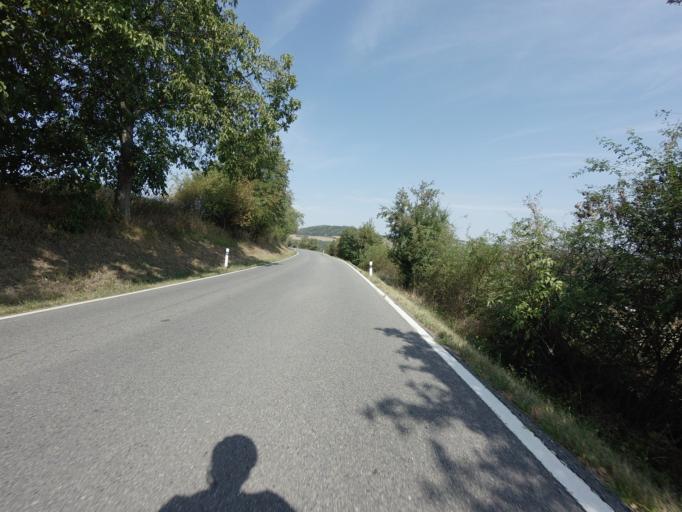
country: CZ
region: Central Bohemia
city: Petrovice
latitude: 49.5898
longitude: 14.3829
